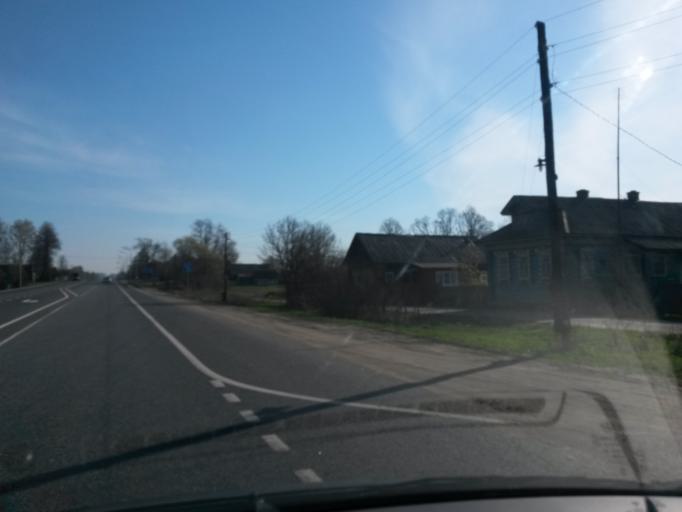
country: RU
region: Jaroslavl
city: Petrovsk
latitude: 56.9348
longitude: 39.1568
